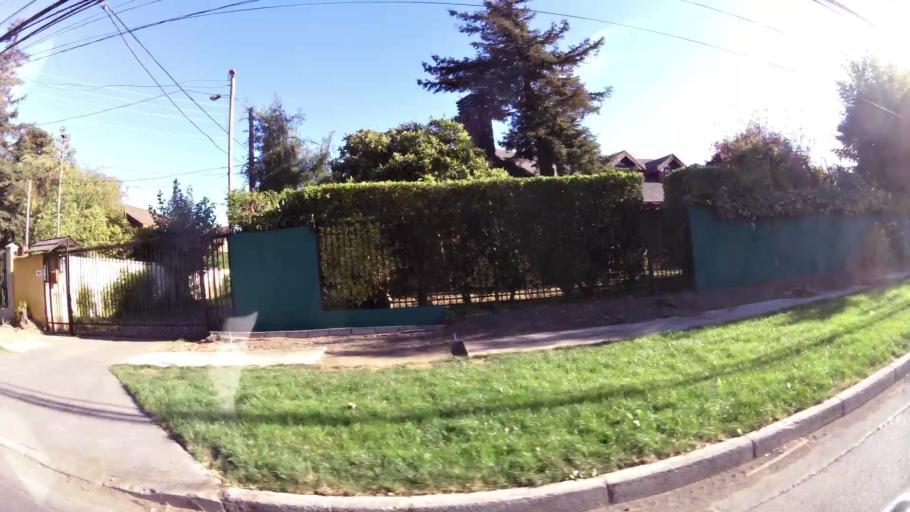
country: CL
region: Biobio
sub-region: Provincia de Concepcion
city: Concepcion
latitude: -36.8348
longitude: -73.1036
